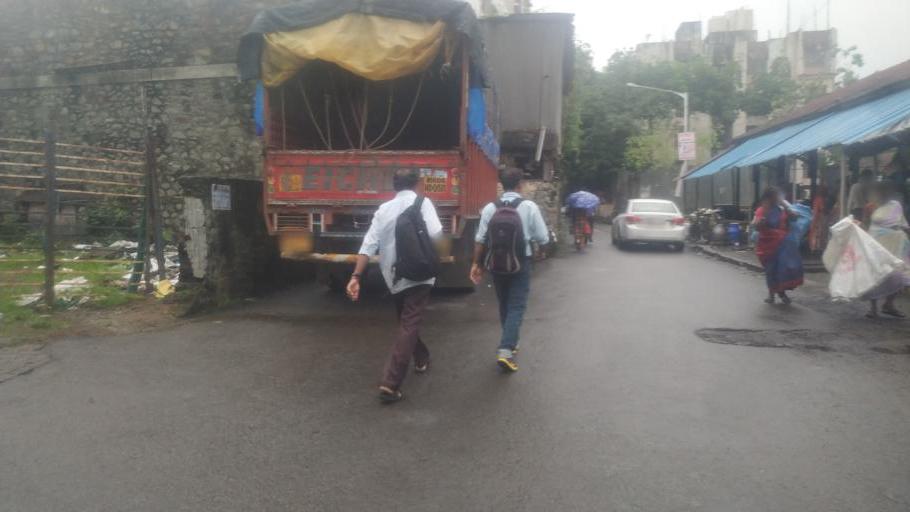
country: IN
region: Maharashtra
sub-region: Mumbai Suburban
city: Powai
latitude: 19.1229
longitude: 72.8498
